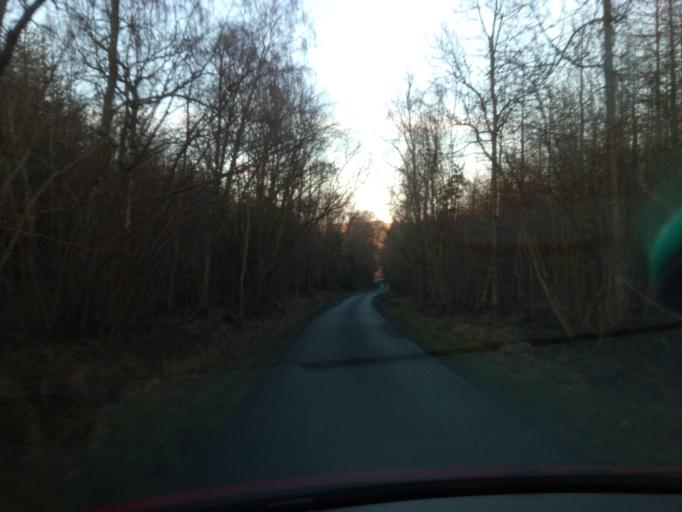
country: GB
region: Scotland
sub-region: The Scottish Borders
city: Melrose
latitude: 55.5855
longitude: -2.7399
